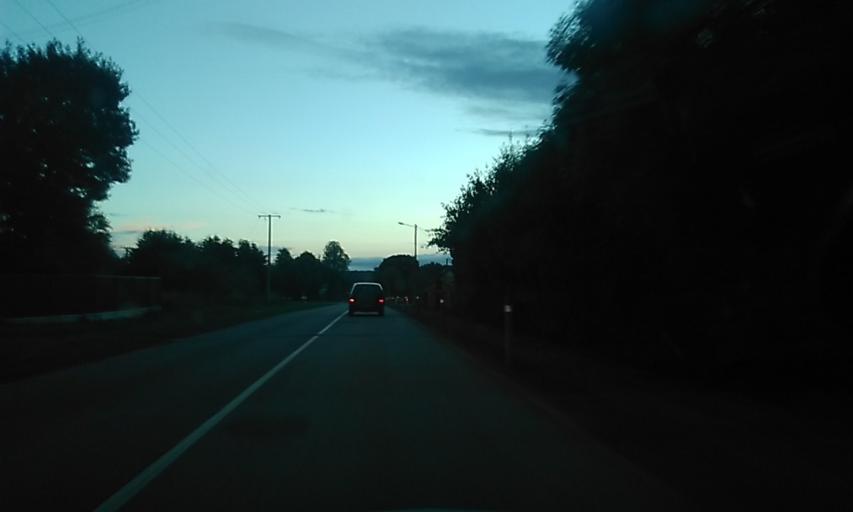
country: FR
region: Brittany
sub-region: Departement d'Ille-et-Vilaine
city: Saint-Thurial
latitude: 48.0485
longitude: -1.9287
